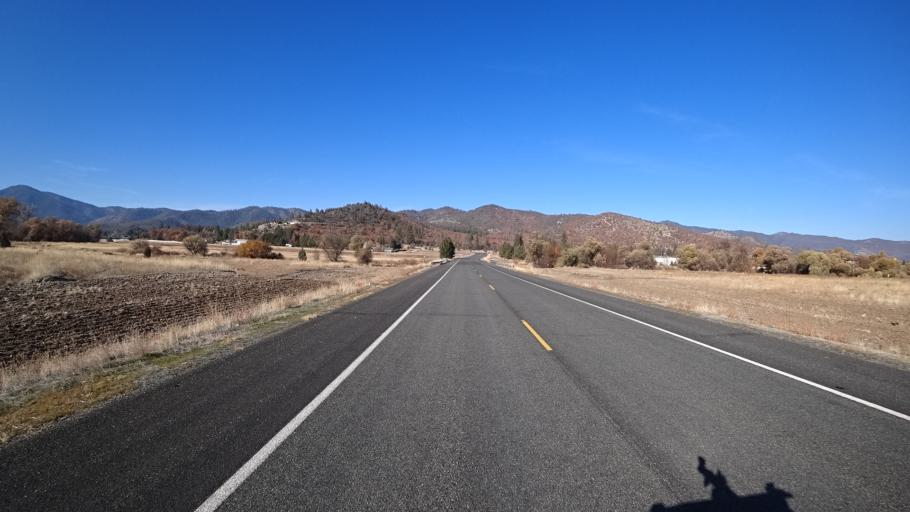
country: US
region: California
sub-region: Siskiyou County
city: Yreka
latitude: 41.6955
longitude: -122.6436
